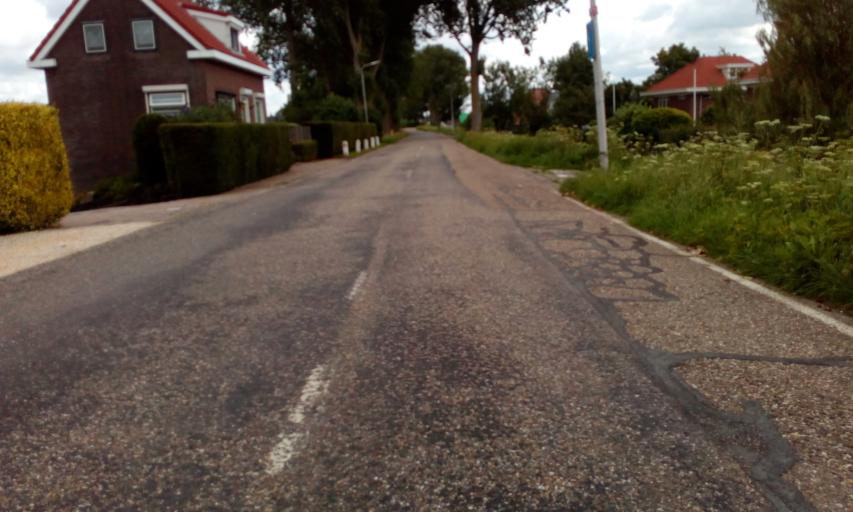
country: NL
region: South Holland
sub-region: Gemeente Binnenmaas
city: Heinenoord
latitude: 51.8575
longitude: 4.4897
